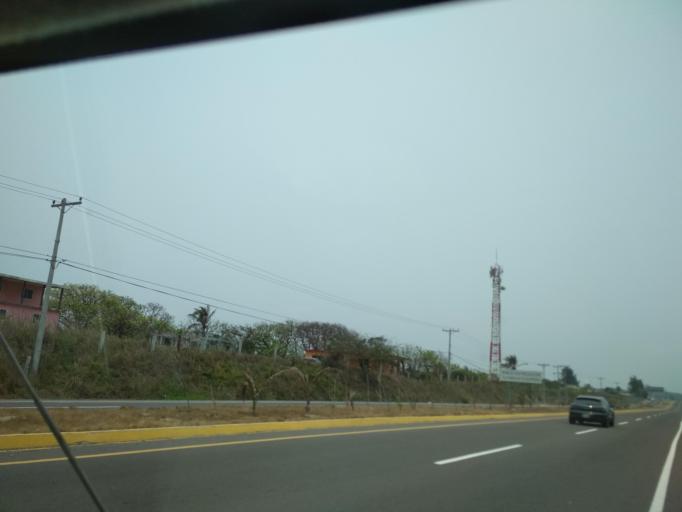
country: MX
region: Veracruz
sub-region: Alvarado
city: Playa de la Libertad
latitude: 19.0560
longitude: -96.0536
